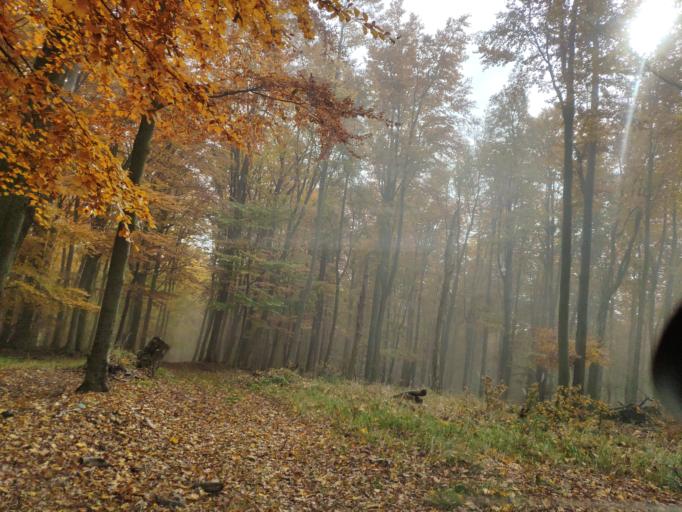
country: SK
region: Kosicky
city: Moldava nad Bodvou
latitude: 48.7319
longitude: 21.0125
